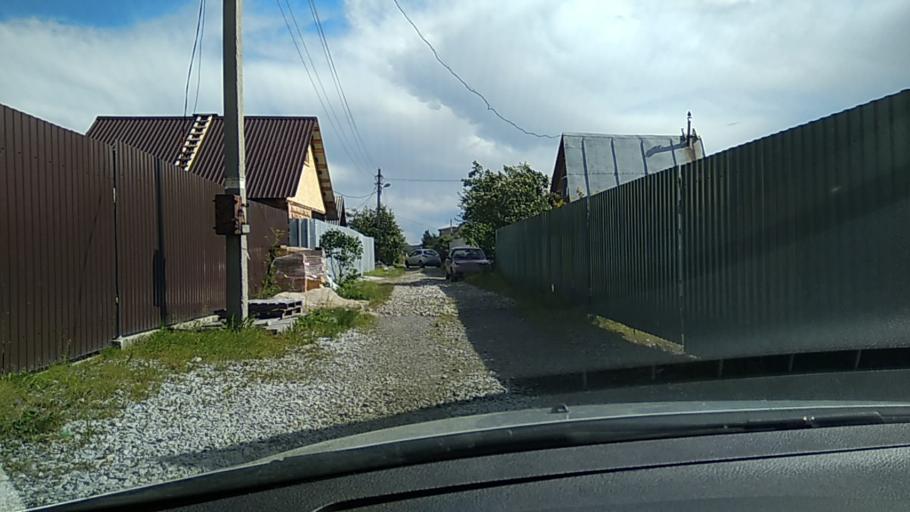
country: RU
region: Sverdlovsk
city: Sredneuralsk
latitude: 56.9710
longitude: 60.4655
